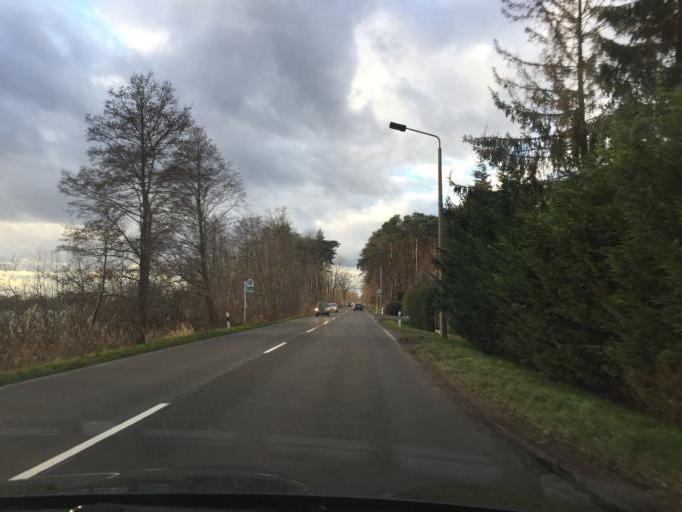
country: DE
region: Brandenburg
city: Kolkwitz
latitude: 51.7504
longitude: 14.2297
